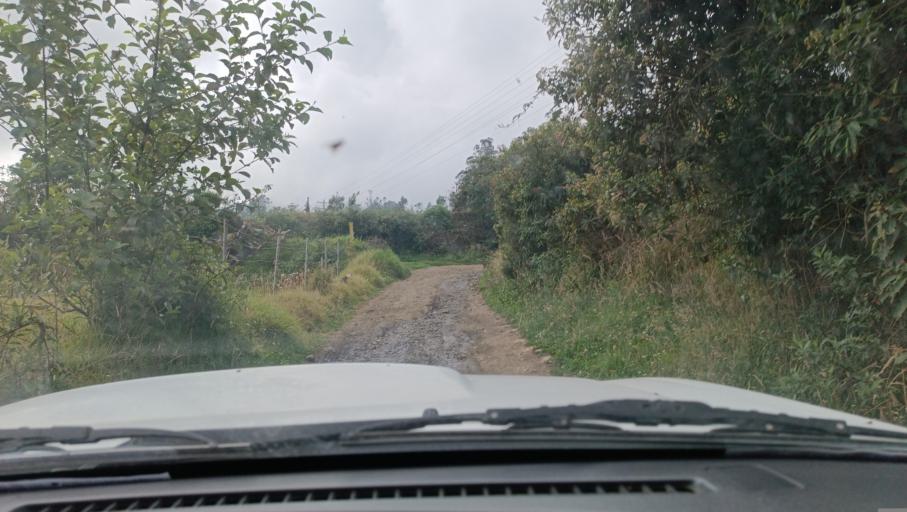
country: EC
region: Chimborazo
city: Riobamba
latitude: -1.6584
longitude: -78.5657
